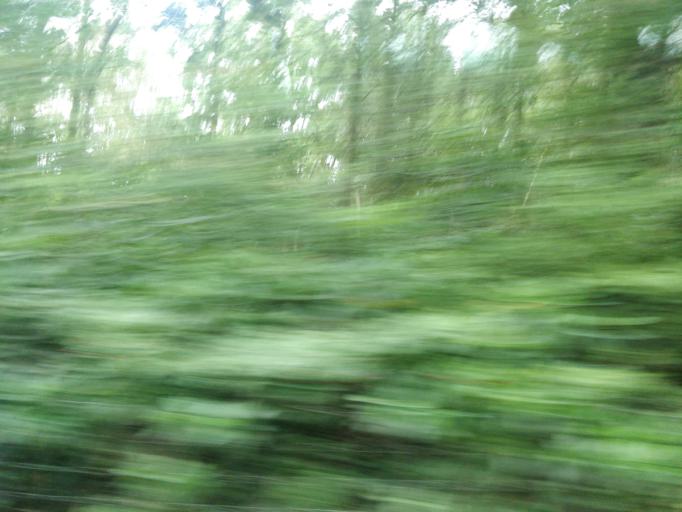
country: GB
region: England
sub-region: Lancashire
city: Ormskirk
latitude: 53.6062
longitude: -2.9133
